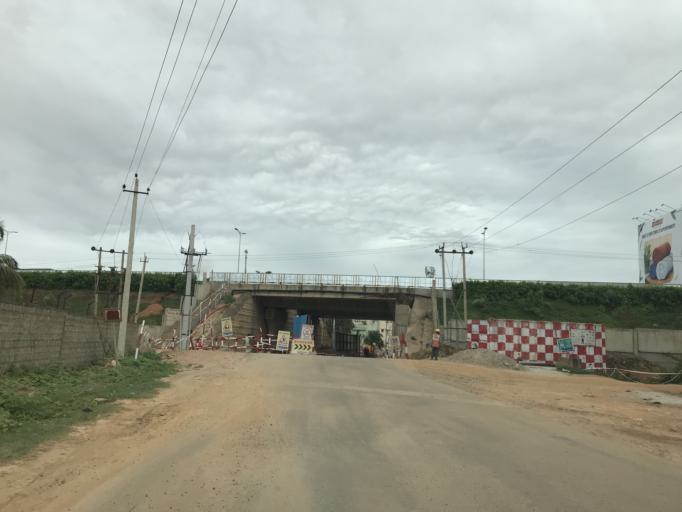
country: IN
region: Karnataka
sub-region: Bangalore Rural
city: Devanhalli
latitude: 13.1988
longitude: 77.6741
